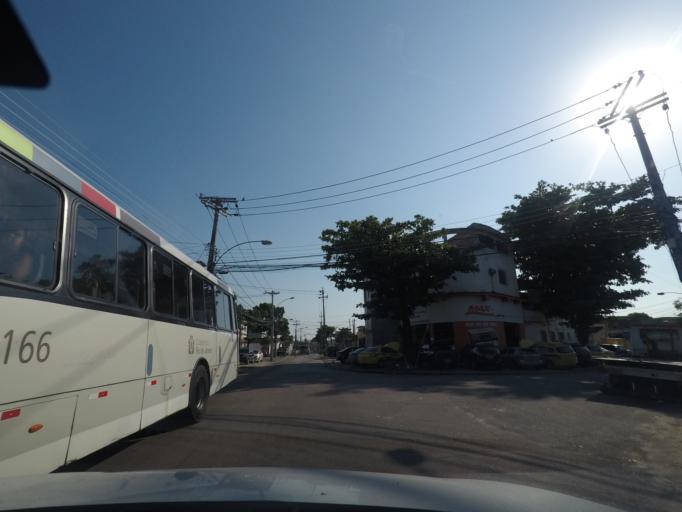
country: BR
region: Rio de Janeiro
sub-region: Duque De Caxias
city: Duque de Caxias
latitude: -22.8251
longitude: -43.2893
